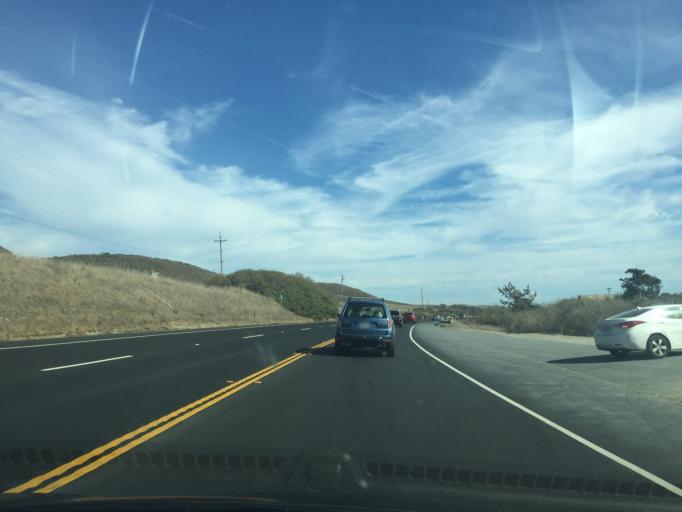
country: US
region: California
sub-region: Santa Cruz County
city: Bonny Doon
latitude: 36.9702
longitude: -122.1196
